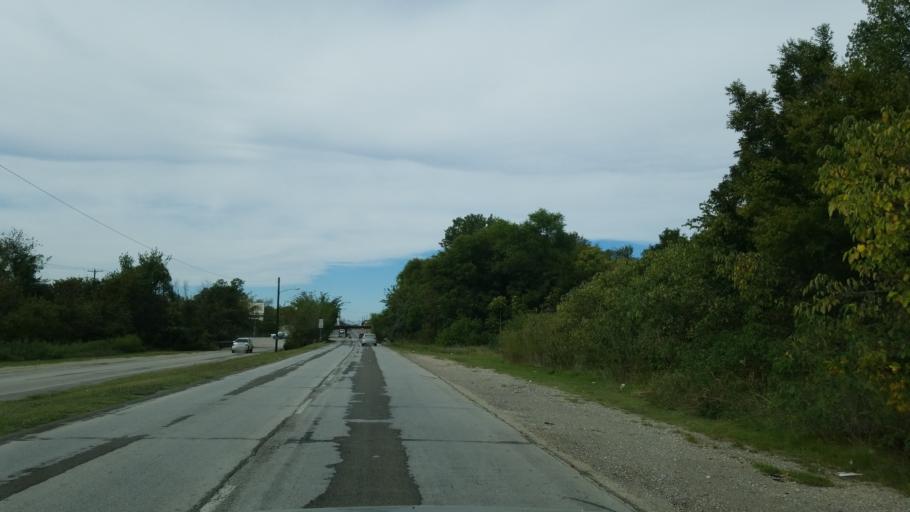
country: US
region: Texas
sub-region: Dallas County
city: Dallas
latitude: 32.7561
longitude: -96.7386
